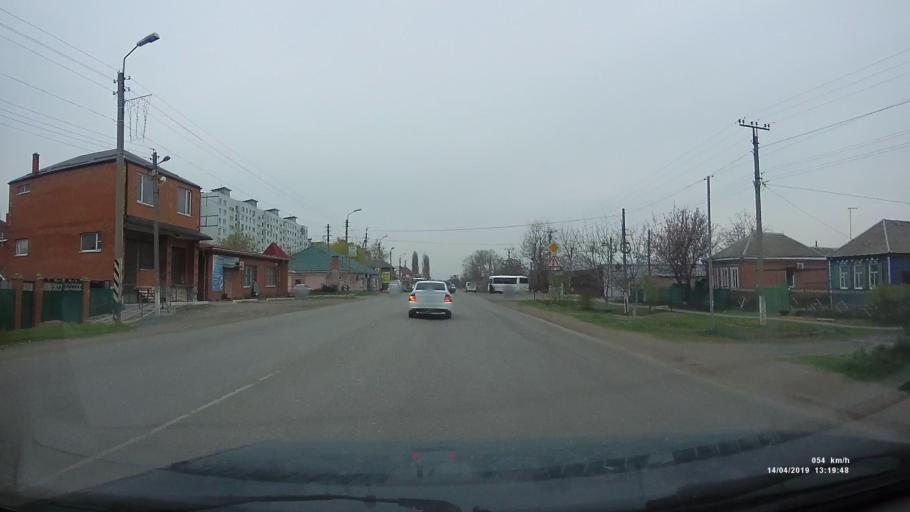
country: RU
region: Rostov
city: Kuleshovka
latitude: 47.0817
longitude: 39.5405
